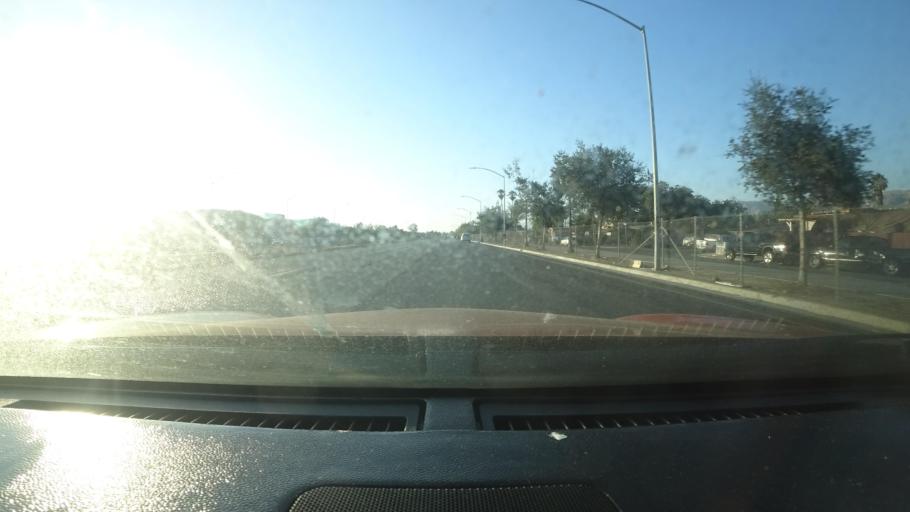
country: US
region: California
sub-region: Santa Clara County
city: Alum Rock
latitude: 37.3467
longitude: -121.8241
